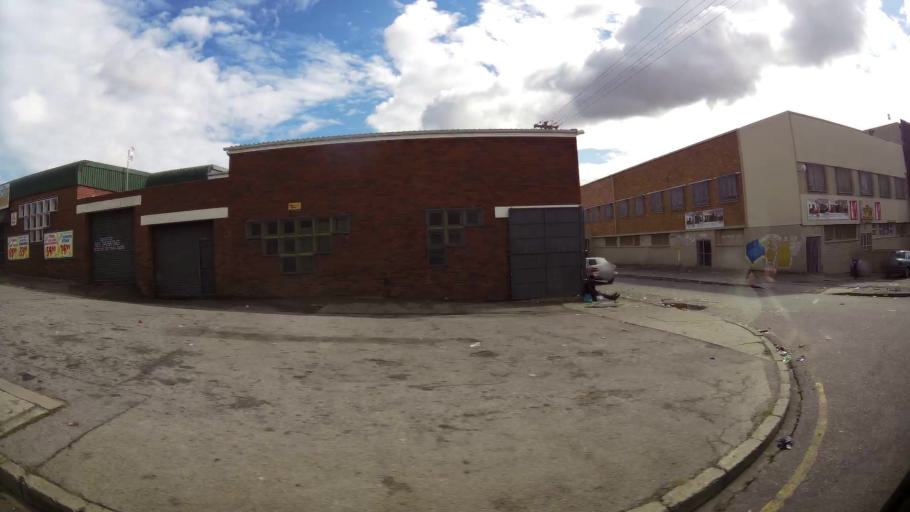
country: ZA
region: Eastern Cape
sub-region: Nelson Mandela Bay Metropolitan Municipality
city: Port Elizabeth
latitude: -33.9286
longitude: 25.5698
